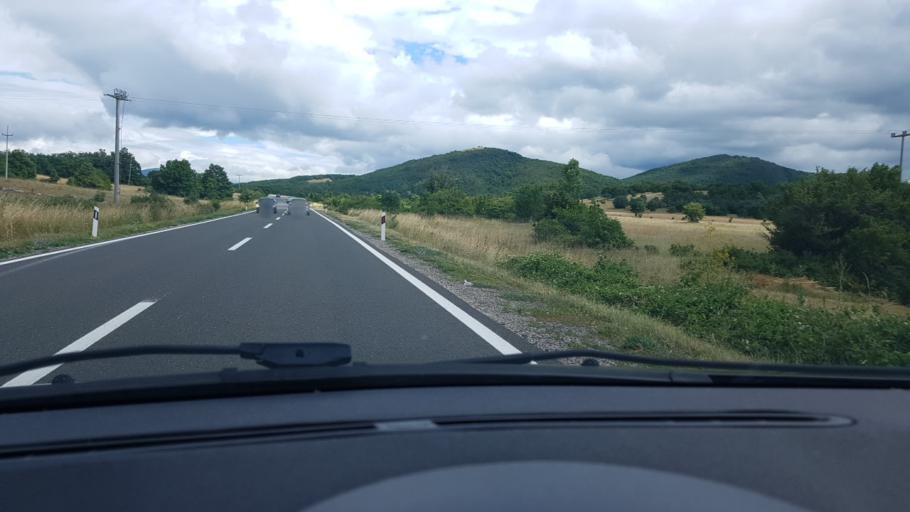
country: HR
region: Zadarska
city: Gracac
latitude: 44.4652
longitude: 15.8022
